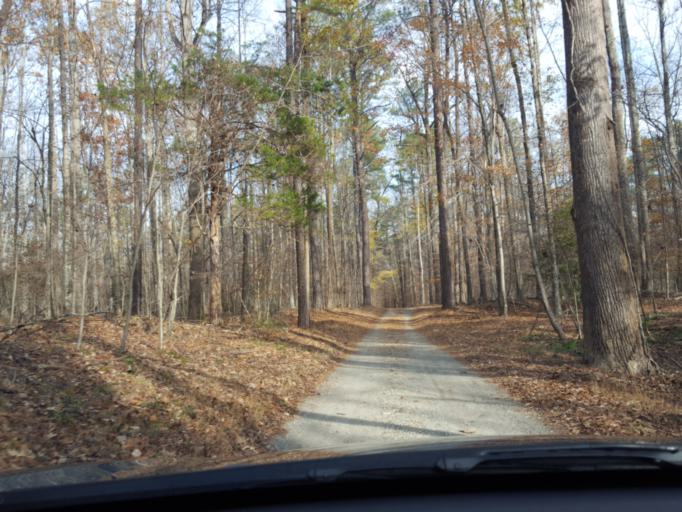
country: US
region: Maryland
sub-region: Calvert County
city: Prince Frederick
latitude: 38.5393
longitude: -76.5581
